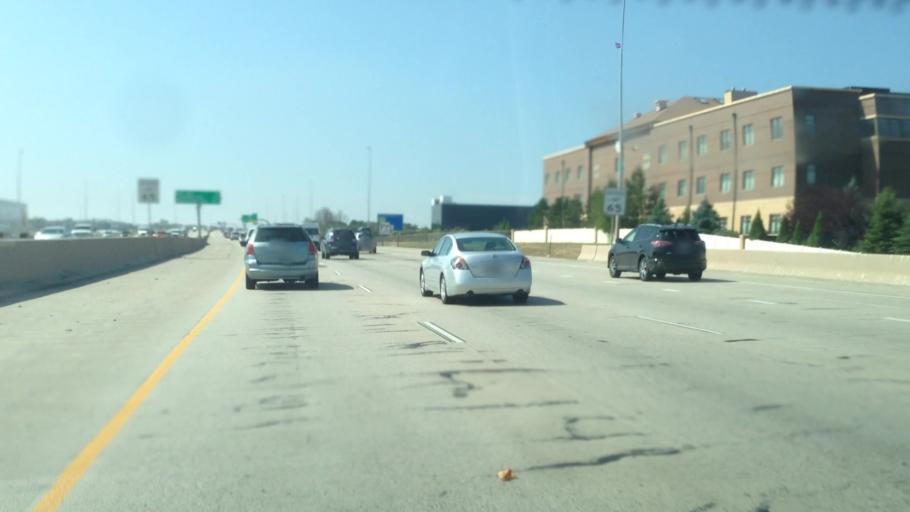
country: US
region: Colorado
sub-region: Adams County
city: Aurora
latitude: 39.7331
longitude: -104.8256
